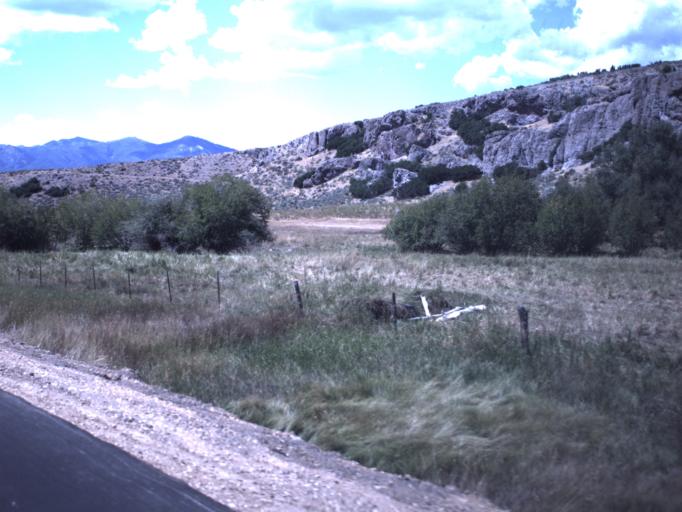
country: US
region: Utah
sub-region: Summit County
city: Francis
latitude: 40.6035
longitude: -111.3232
